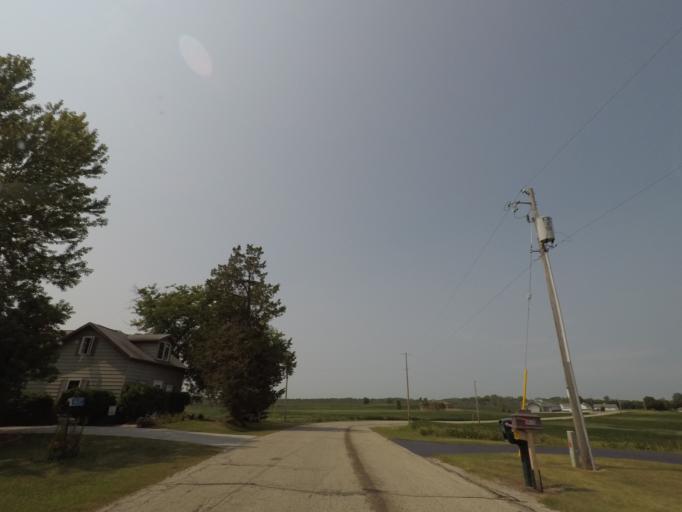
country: US
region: Wisconsin
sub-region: Waukesha County
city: Oconomowoc
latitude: 43.0653
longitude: -88.5654
